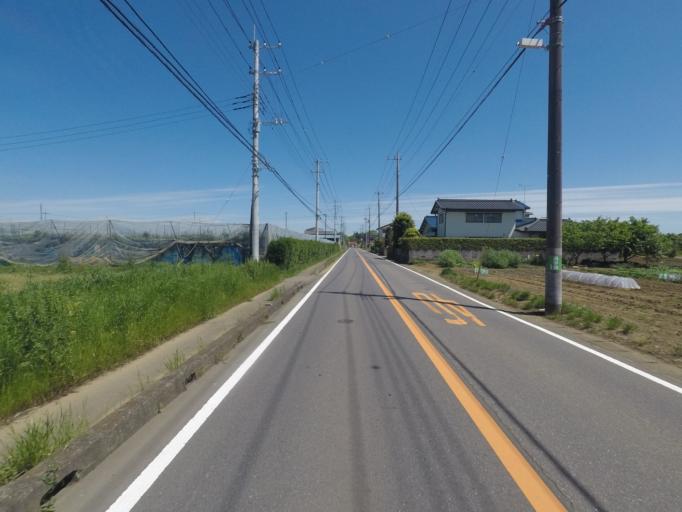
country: JP
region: Ibaraki
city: Ami
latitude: 36.1004
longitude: 140.2344
